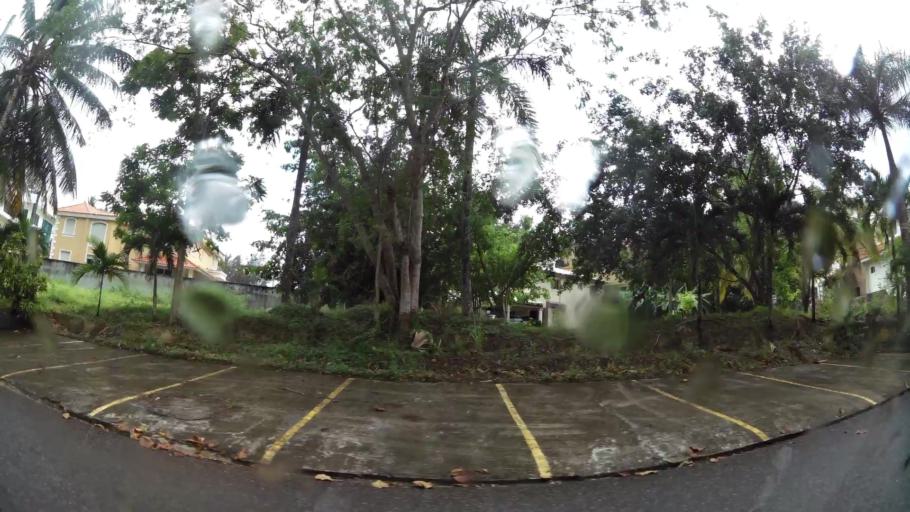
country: DO
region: Nacional
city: La Agustina
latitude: 18.5144
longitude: -69.9340
